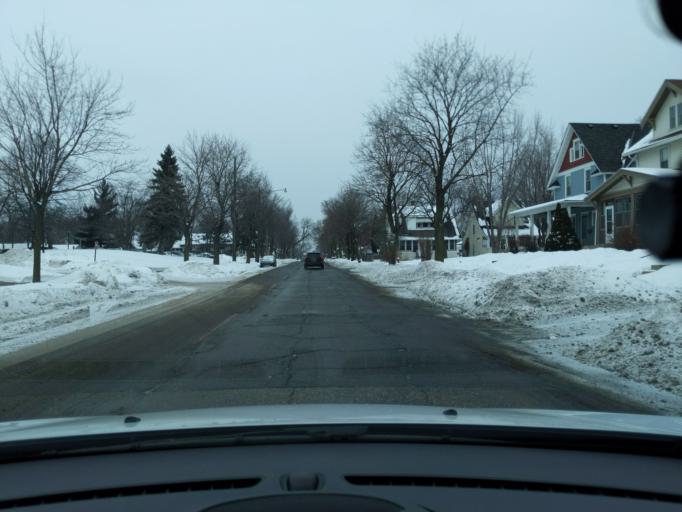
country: US
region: Minnesota
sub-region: Ramsey County
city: Falcon Heights
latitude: 44.9642
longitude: -93.1569
